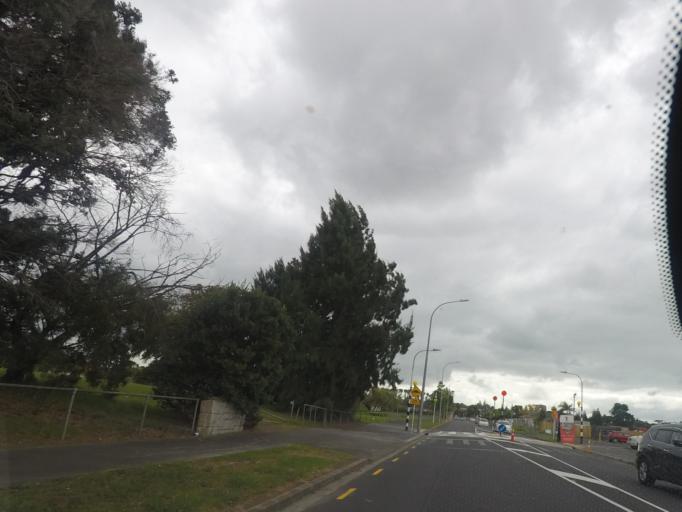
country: NZ
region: Auckland
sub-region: Auckland
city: Tamaki
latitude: -36.8801
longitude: 174.8658
